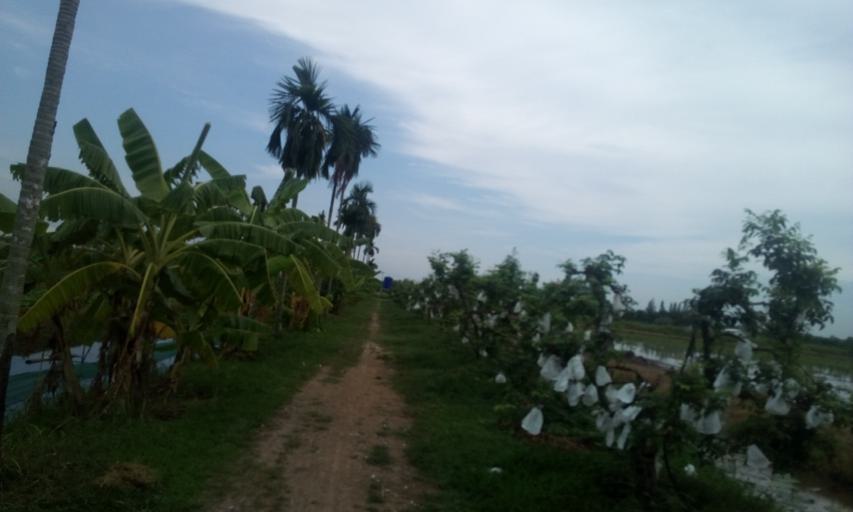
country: TH
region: Pathum Thani
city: Ban Lam Luk Ka
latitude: 13.9896
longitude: 100.8365
